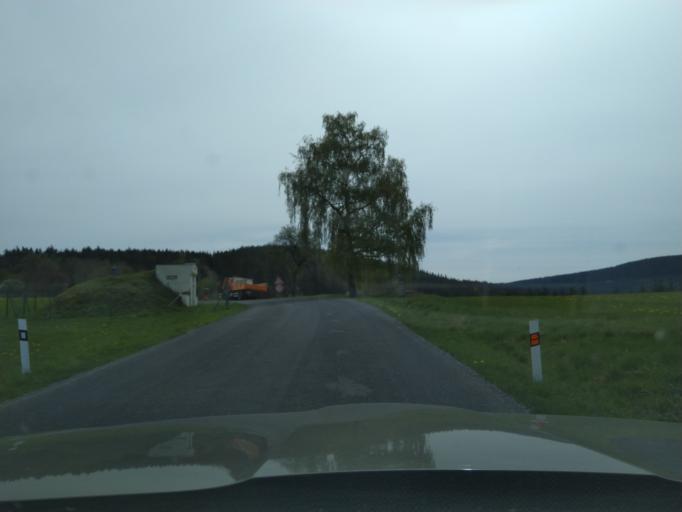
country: CZ
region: Jihocesky
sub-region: Okres Prachatice
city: Stachy
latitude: 49.1799
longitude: 13.6529
